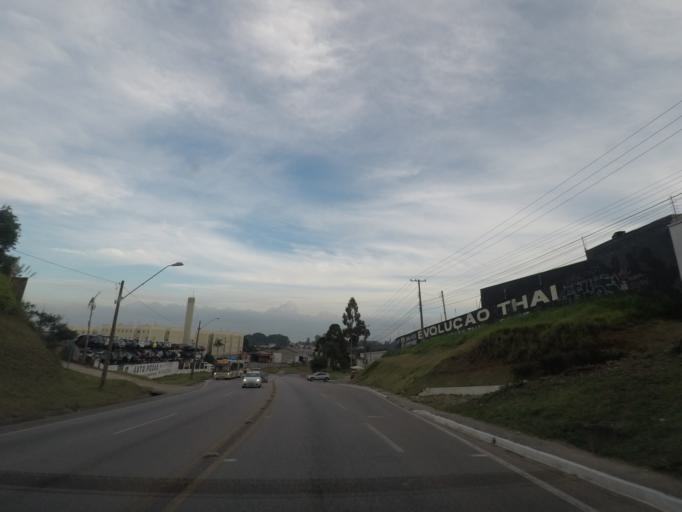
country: BR
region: Parana
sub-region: Colombo
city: Colombo
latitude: -25.3594
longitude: -49.2195
